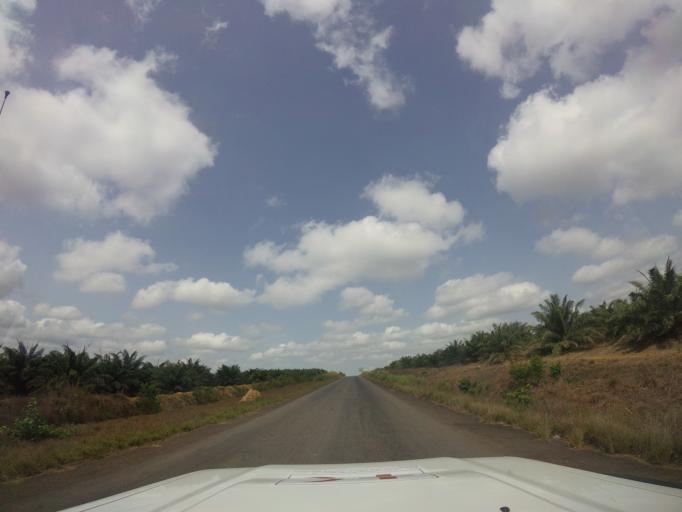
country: LR
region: Bomi
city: Tubmanburg
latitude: 6.7286
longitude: -11.0267
